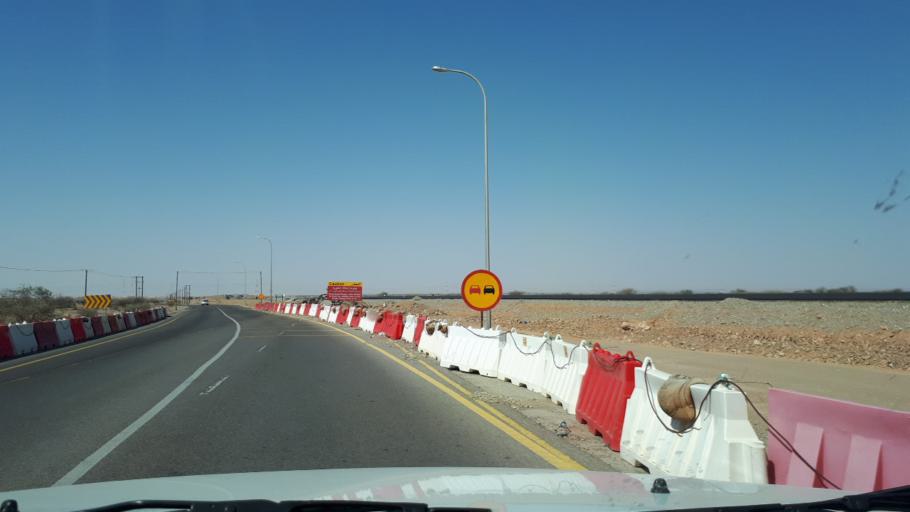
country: OM
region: Ash Sharqiyah
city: Sur
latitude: 22.2954
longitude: 59.2793
